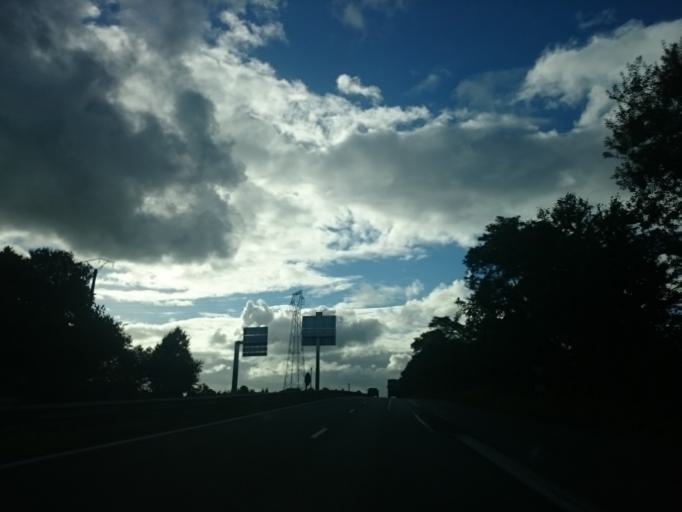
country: FR
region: Brittany
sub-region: Departement des Cotes-d'Armor
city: Graces
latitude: 48.5653
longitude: -3.2122
